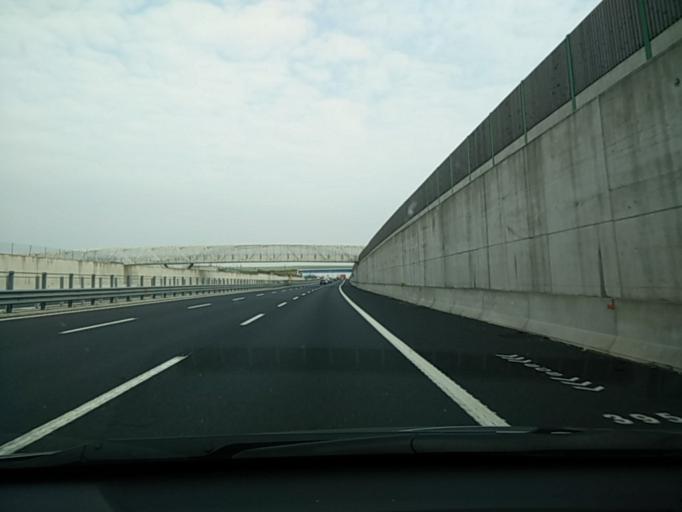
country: IT
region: Veneto
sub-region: Provincia di Treviso
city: Sambughe
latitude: 45.5894
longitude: 12.2137
